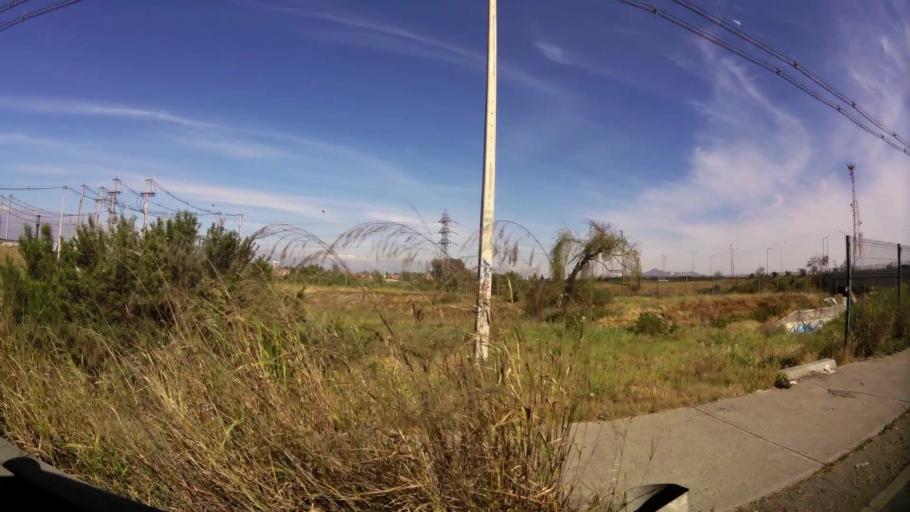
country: CL
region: Santiago Metropolitan
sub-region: Provincia de Santiago
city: Lo Prado
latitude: -33.4876
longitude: -70.7493
